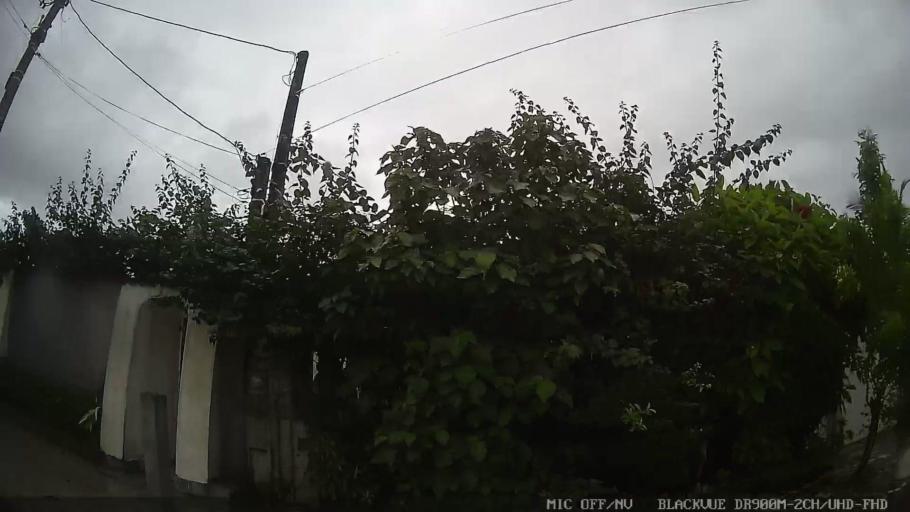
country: BR
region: Sao Paulo
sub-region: Itanhaem
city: Itanhaem
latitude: -24.1782
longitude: -46.8186
